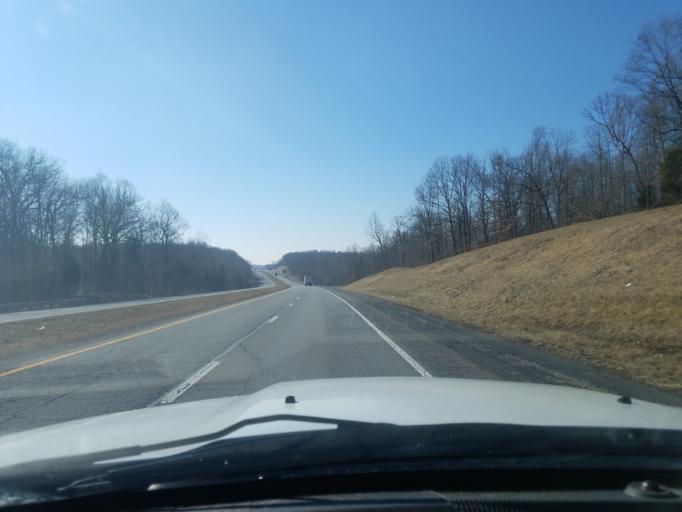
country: US
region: Kentucky
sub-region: Hardin County
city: Elizabethtown
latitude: 37.6704
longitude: -85.8759
